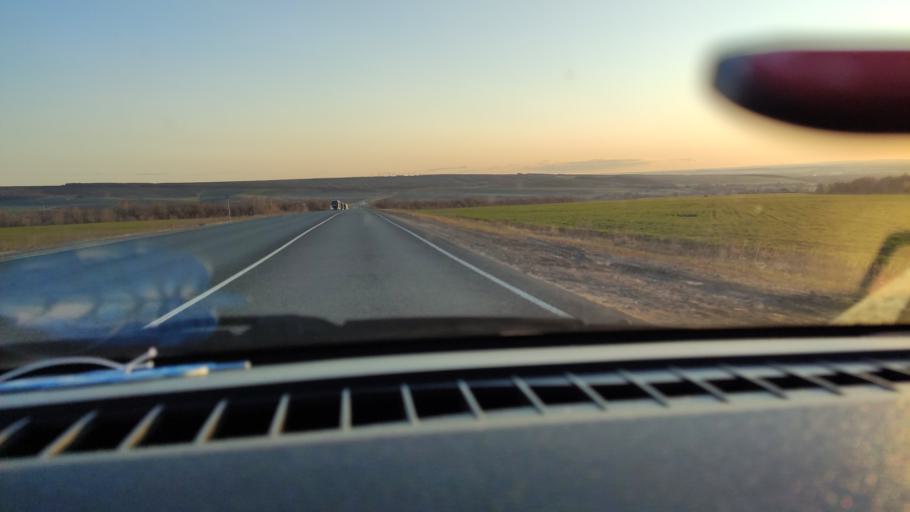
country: RU
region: Saratov
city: Sinodskoye
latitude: 51.9066
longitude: 46.5500
